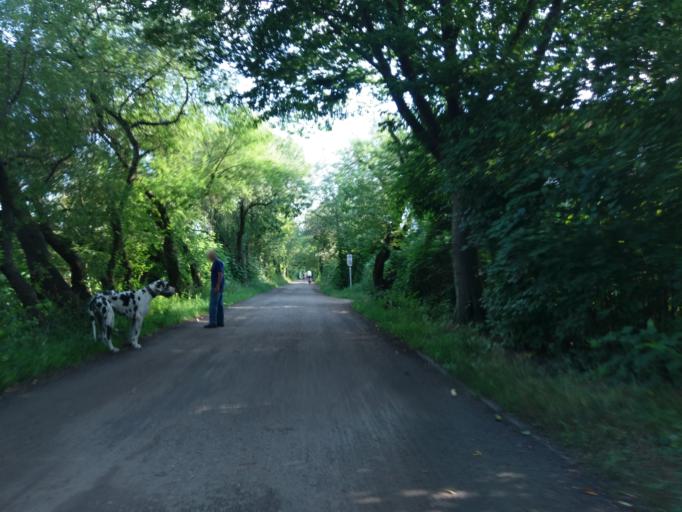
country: DE
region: Berlin
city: Lichterfelde
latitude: 52.4226
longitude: 13.3043
